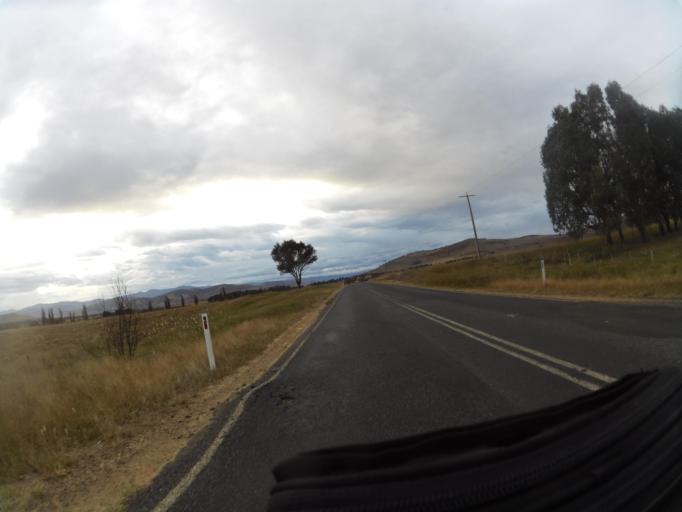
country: AU
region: New South Wales
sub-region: Greater Hume Shire
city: Holbrook
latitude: -36.0602
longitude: 147.9449
